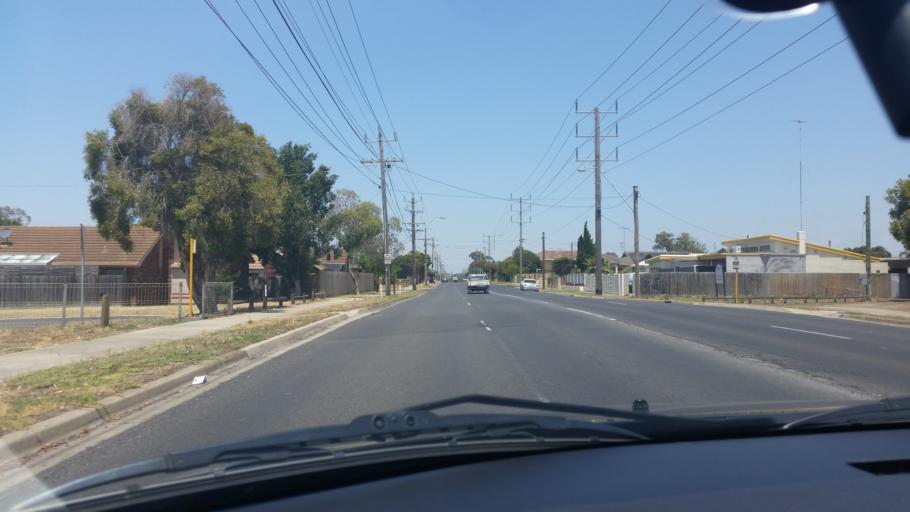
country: AU
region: Victoria
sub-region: Greater Geelong
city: Bell Park
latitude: -38.1144
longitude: 144.3427
